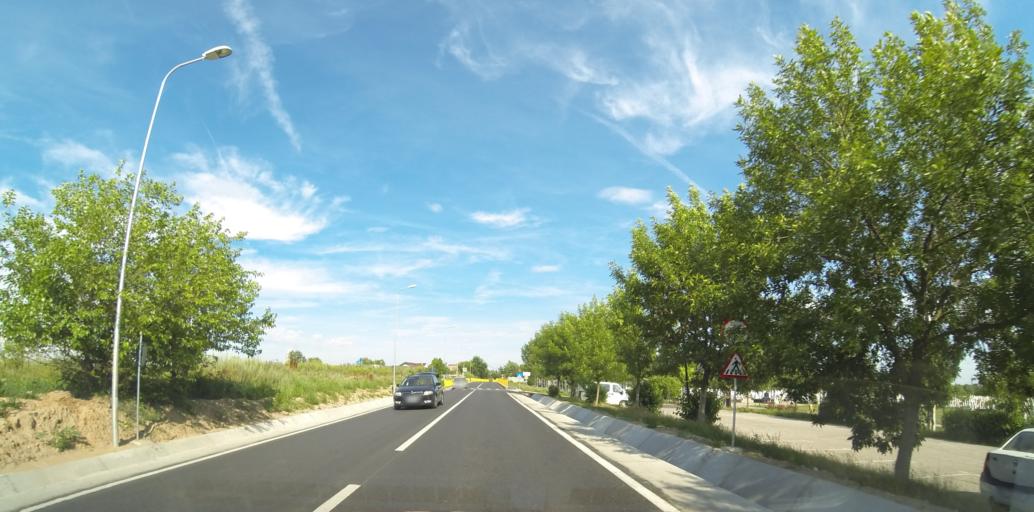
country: RO
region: Dolj
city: Craiova
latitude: 44.3420
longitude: 23.7915
